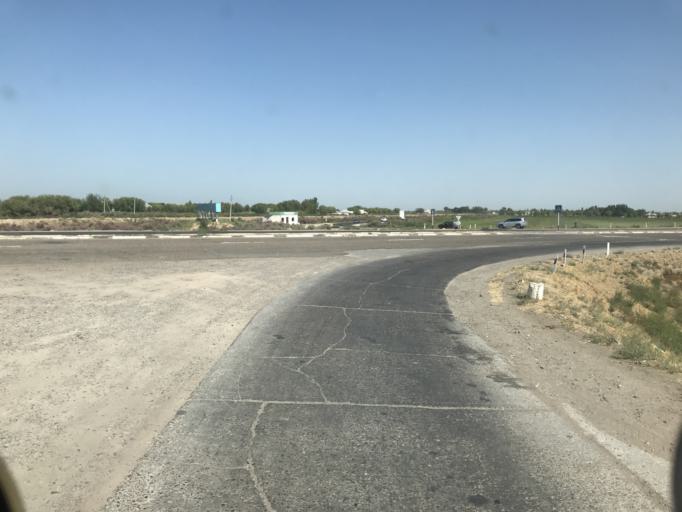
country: KZ
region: Ongtustik Qazaqstan
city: Myrzakent
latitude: 40.7485
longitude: 68.5377
